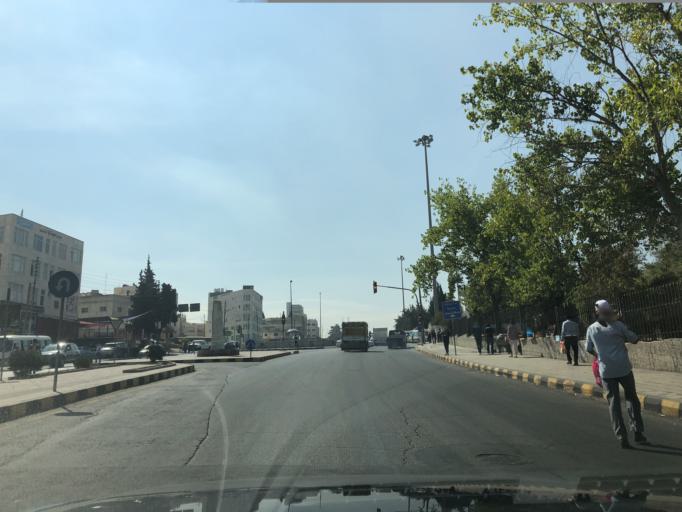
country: JO
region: Amman
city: Al Jubayhah
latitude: 32.0214
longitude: 35.8439
